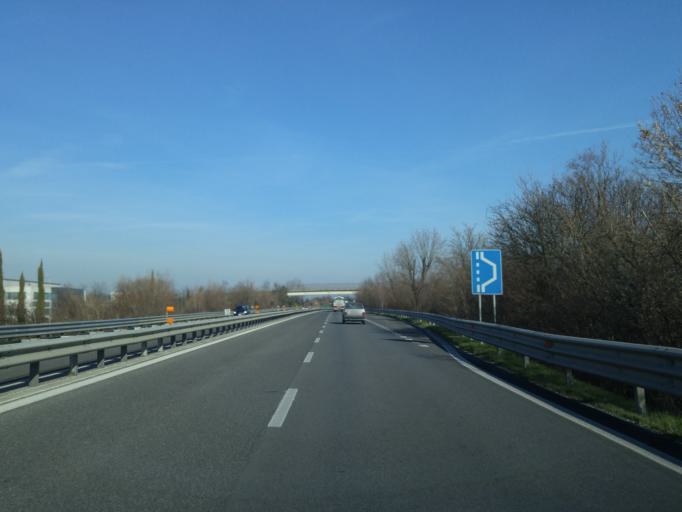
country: IT
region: The Marches
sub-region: Provincia di Pesaro e Urbino
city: Lucrezia
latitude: 43.7606
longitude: 12.9375
